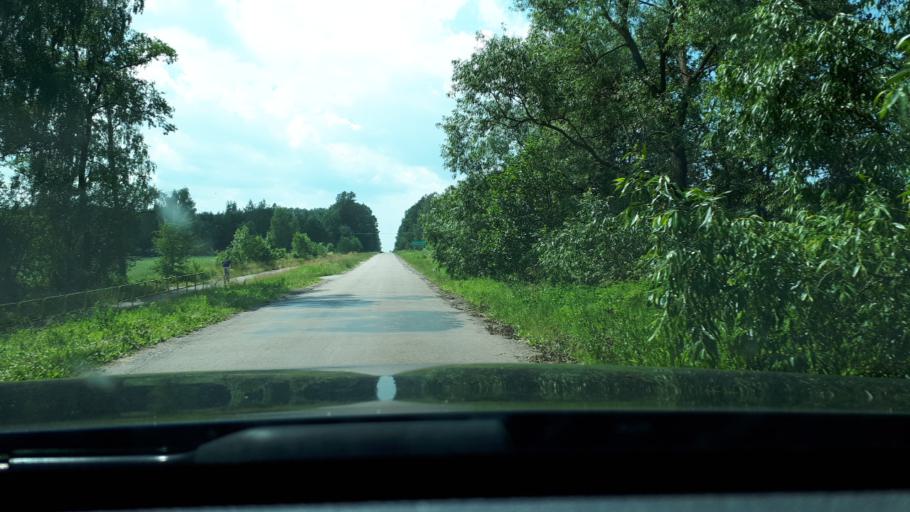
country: PL
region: Podlasie
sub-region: Powiat bialostocki
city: Choroszcz
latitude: 53.1223
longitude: 22.9239
